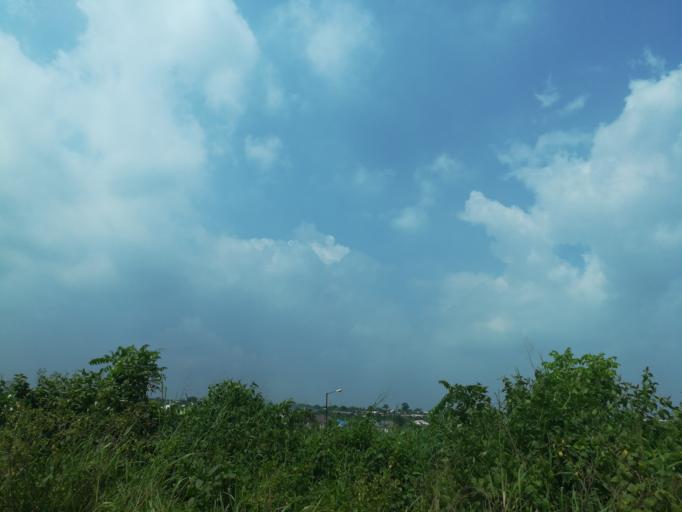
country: NG
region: Lagos
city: Ikorodu
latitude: 6.5979
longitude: 3.6308
